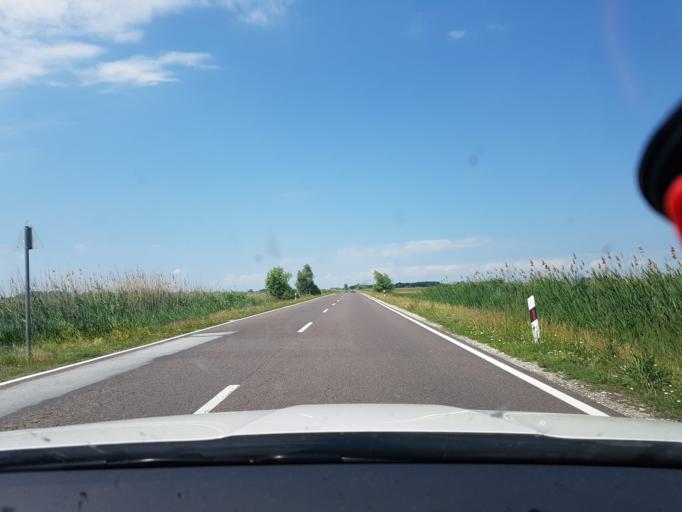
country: HU
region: Hajdu-Bihar
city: Egyek
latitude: 47.5524
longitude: 20.8782
